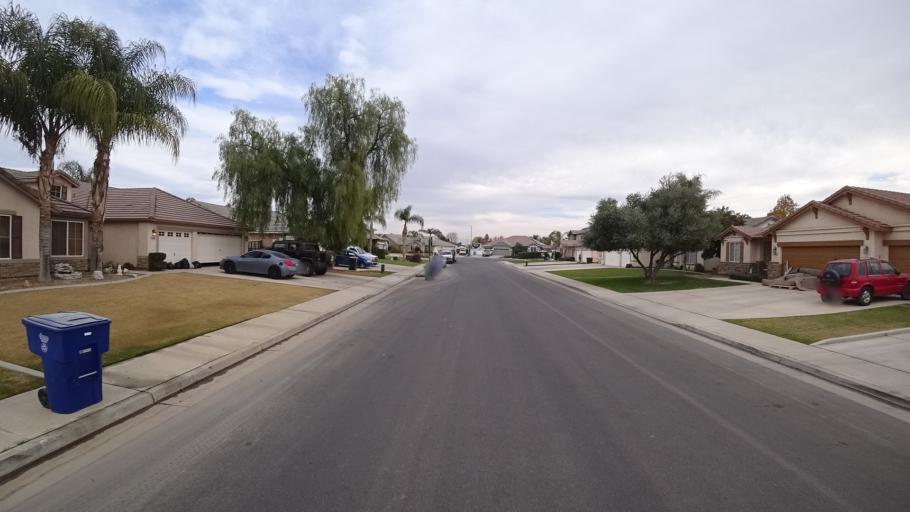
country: US
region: California
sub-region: Kern County
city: Rosedale
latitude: 35.4261
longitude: -119.1334
